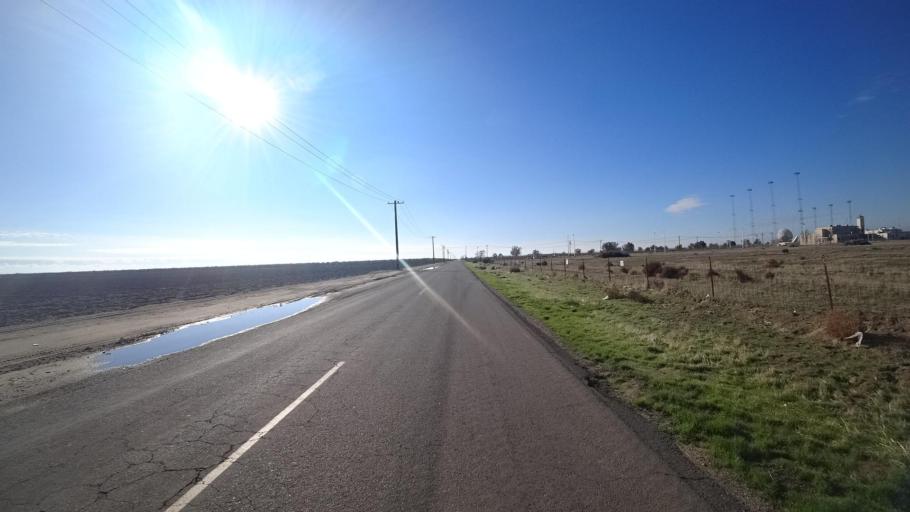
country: US
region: California
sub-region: Kern County
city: Delano
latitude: 35.7563
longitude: -119.2768
